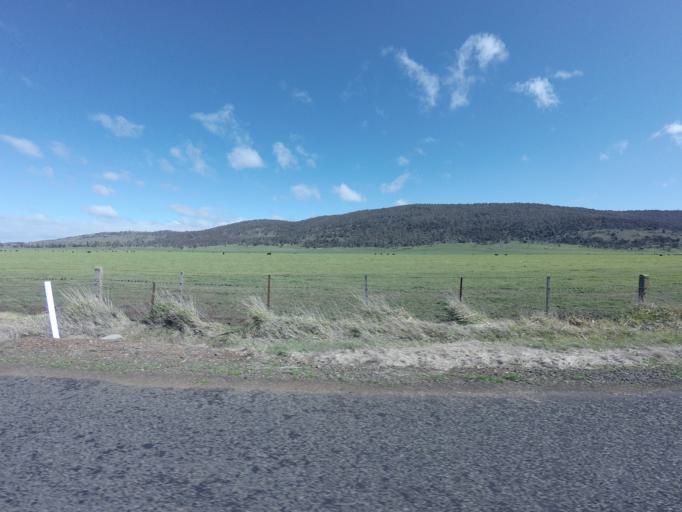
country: AU
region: Tasmania
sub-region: Northern Midlands
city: Evandale
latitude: -41.9762
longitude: 147.4460
